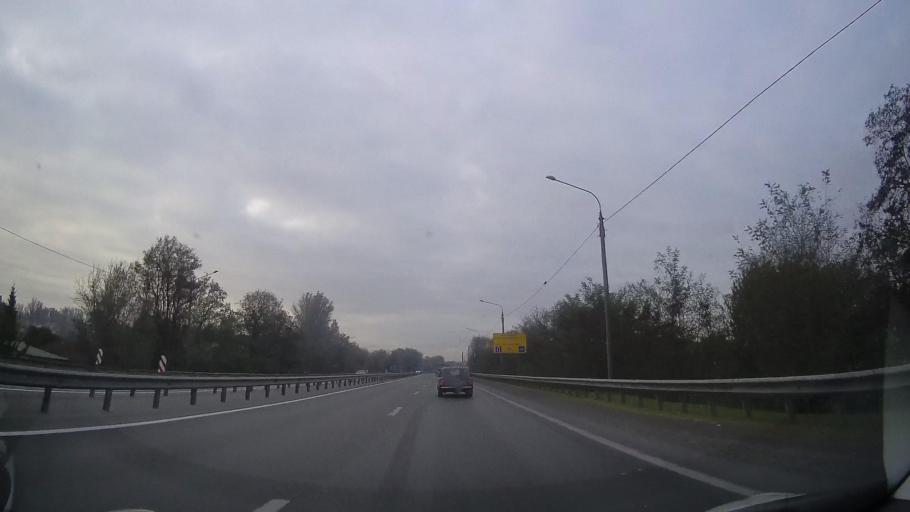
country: RU
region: Rostov
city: Bataysk
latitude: 47.1301
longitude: 39.7750
